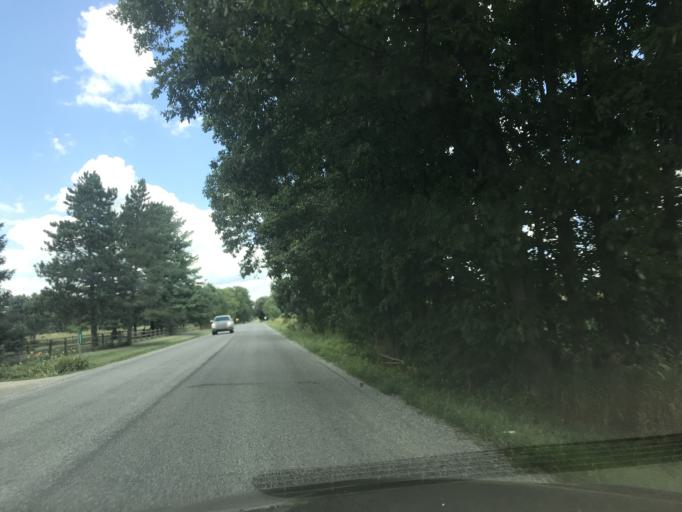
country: US
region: Michigan
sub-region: Ingham County
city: Holt
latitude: 42.6041
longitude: -84.5625
